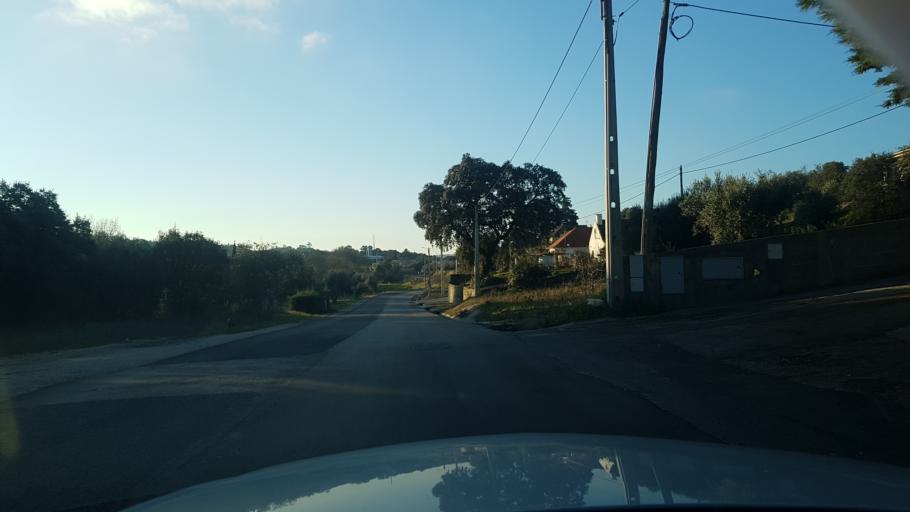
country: PT
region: Santarem
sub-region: Torres Novas
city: Torres Novas
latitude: 39.5504
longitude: -8.5521
